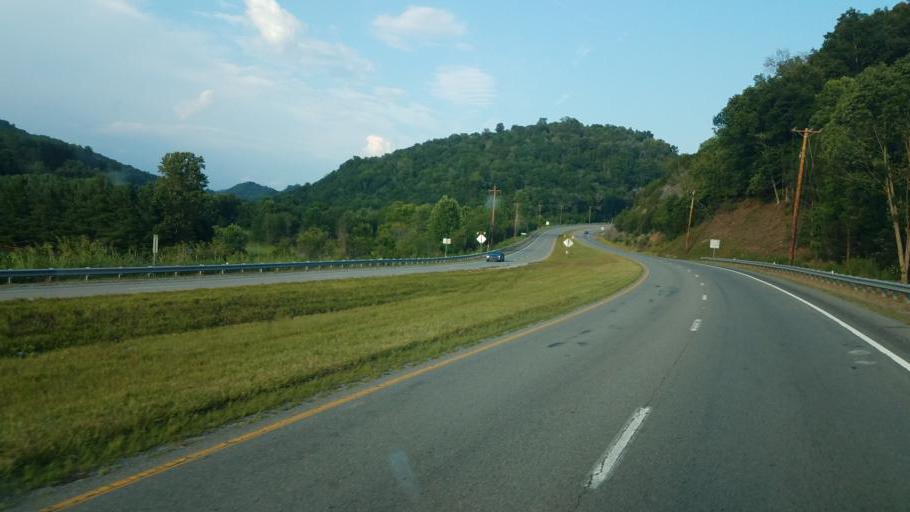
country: US
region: Virginia
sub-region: Lee County
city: Dryden
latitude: 36.7105
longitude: -82.7892
